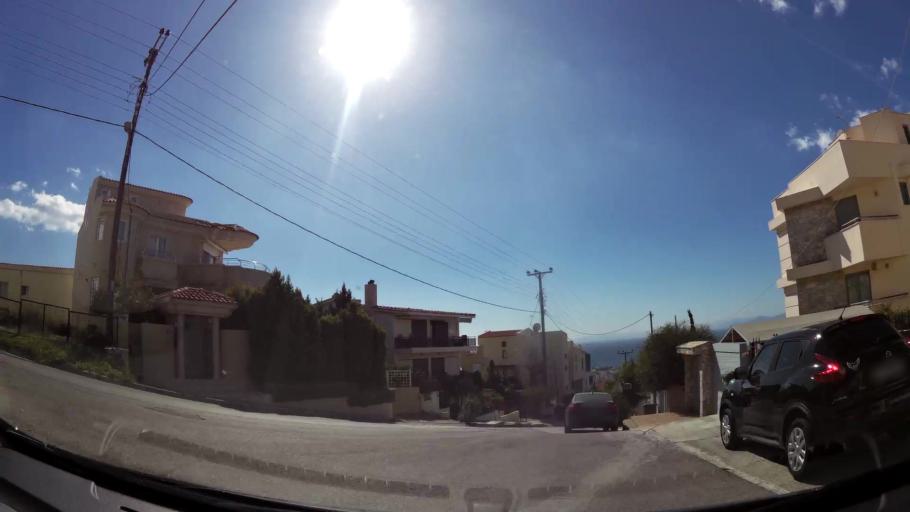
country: GR
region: Attica
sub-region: Nomarchia Anatolikis Attikis
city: Voula
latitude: 37.8559
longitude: 23.7779
